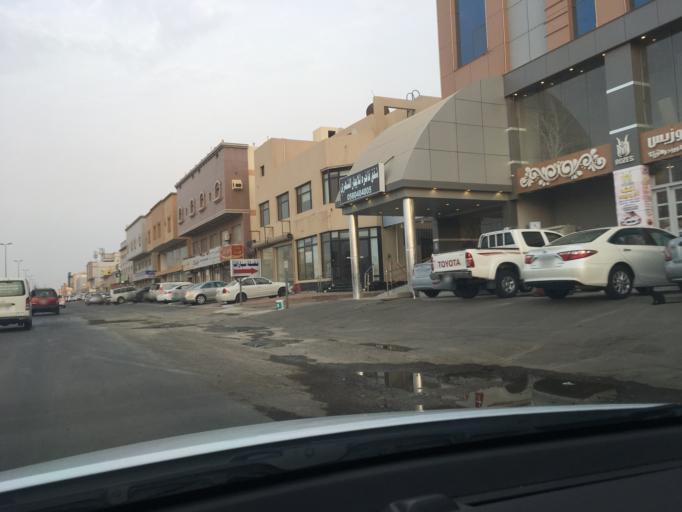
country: SA
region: Makkah
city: Jeddah
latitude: 21.7601
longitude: 39.1944
